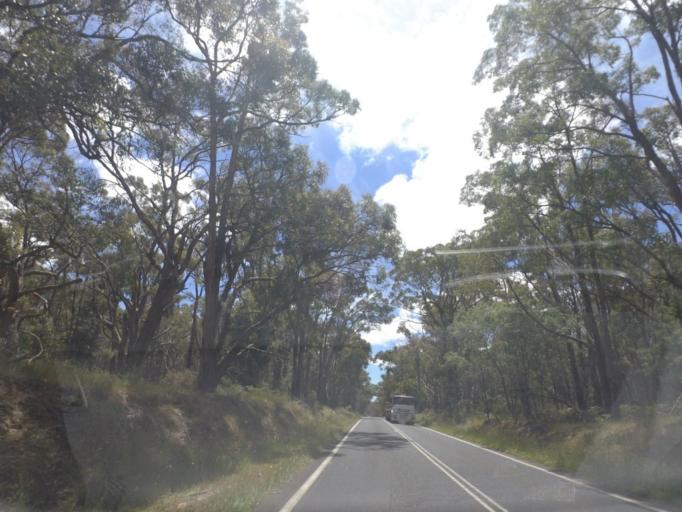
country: AU
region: Victoria
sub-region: Mount Alexander
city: Castlemaine
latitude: -37.3096
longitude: 144.1653
